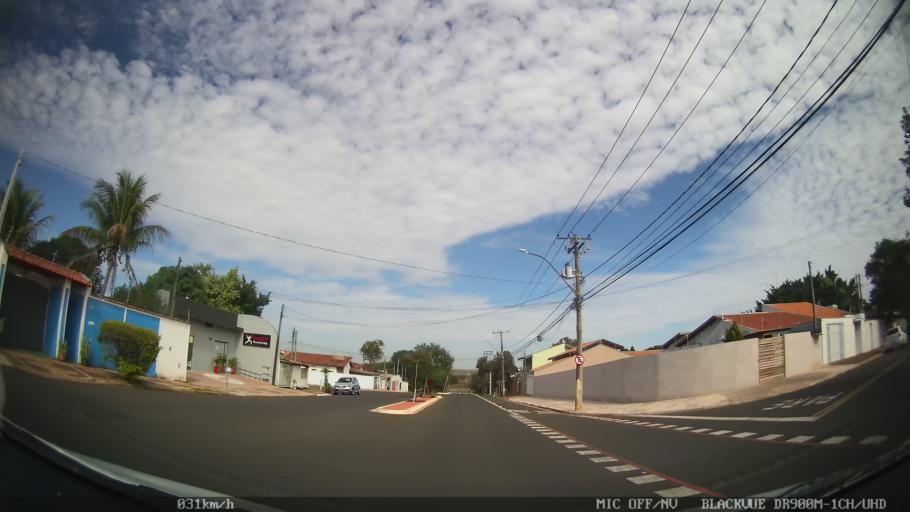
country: BR
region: Sao Paulo
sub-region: Santa Barbara D'Oeste
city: Santa Barbara d'Oeste
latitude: -22.7648
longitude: -47.4288
